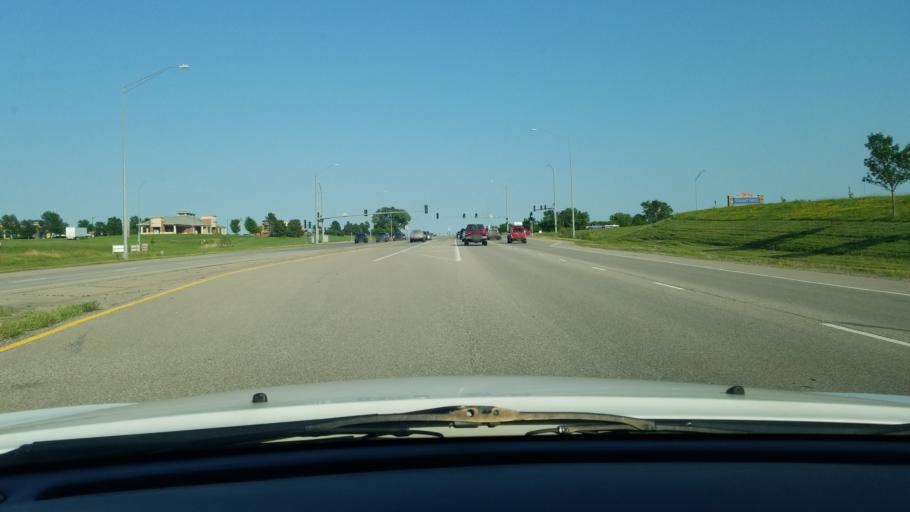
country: US
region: Nebraska
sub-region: Lancaster County
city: Lincoln
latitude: 40.7367
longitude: -96.6079
